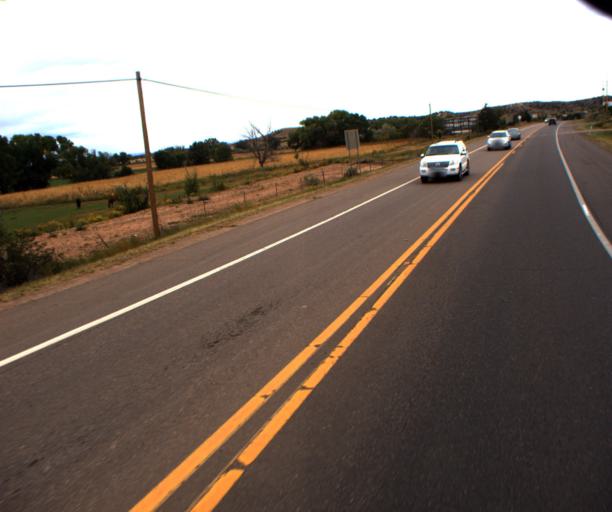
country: US
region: Arizona
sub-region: Navajo County
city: Taylor
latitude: 34.4577
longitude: -110.0912
